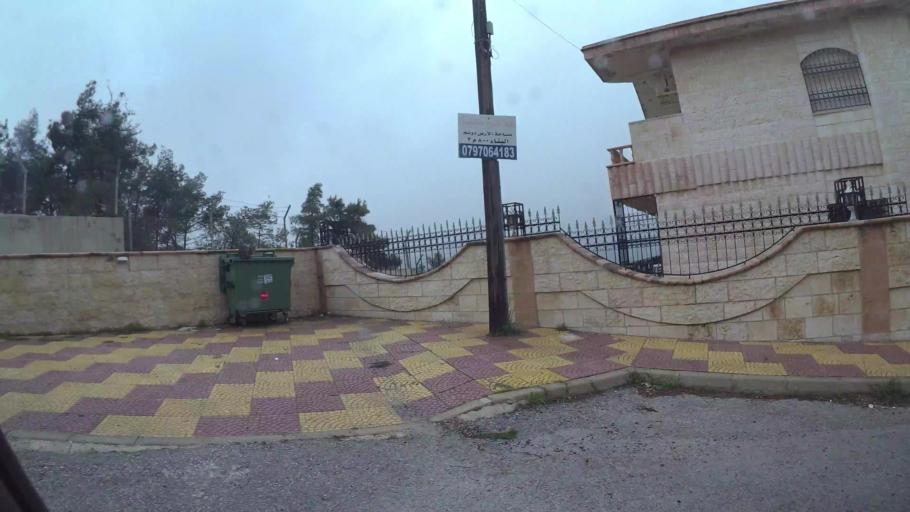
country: JO
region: Amman
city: Al Jubayhah
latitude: 32.0251
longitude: 35.8262
